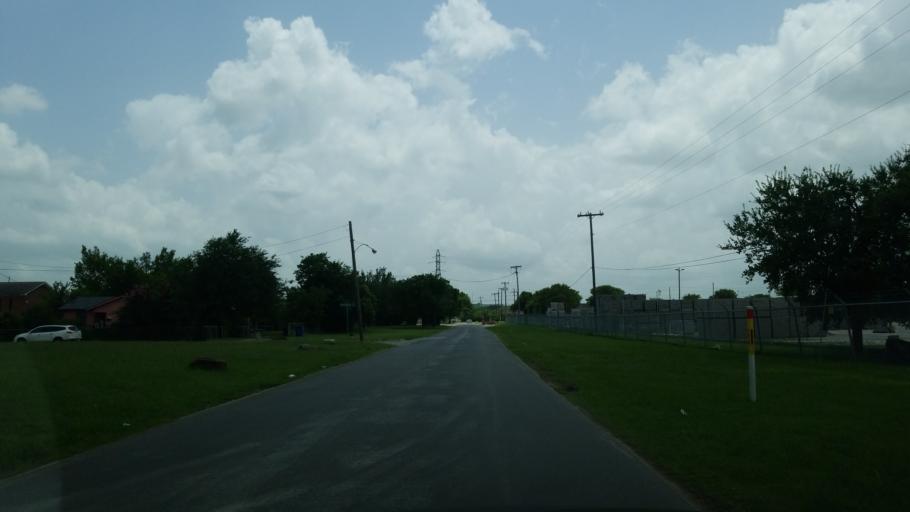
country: US
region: Texas
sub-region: Dallas County
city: Cockrell Hill
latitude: 32.7813
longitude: -96.8826
